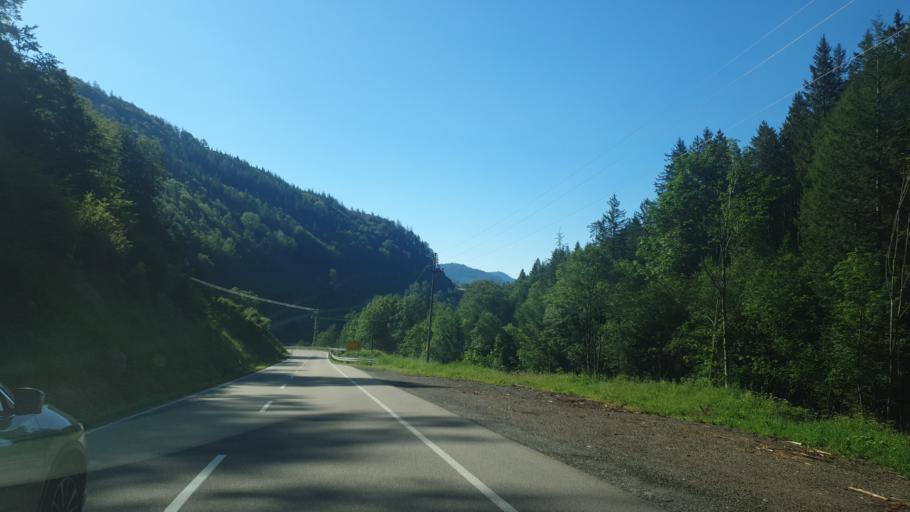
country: DE
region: Baden-Wuerttemberg
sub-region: Freiburg Region
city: Todtnau
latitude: 47.8529
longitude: 7.9196
